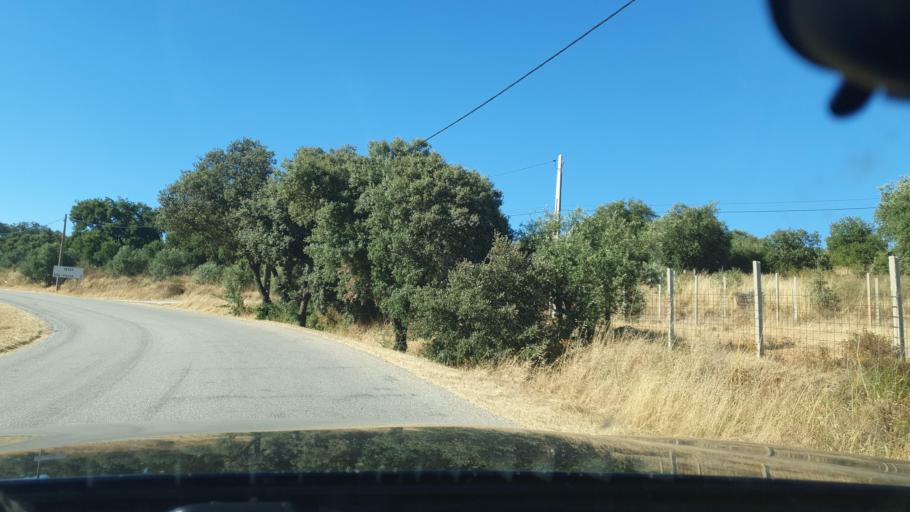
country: PT
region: Evora
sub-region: Alandroal
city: Alandroal
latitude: 38.7089
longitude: -7.4056
